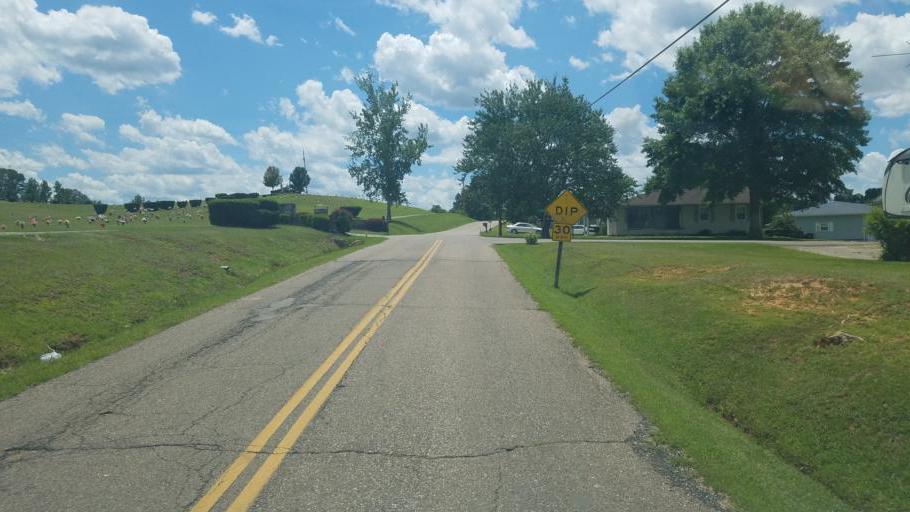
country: US
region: Ohio
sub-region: Gallia County
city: Gallipolis
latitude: 38.7920
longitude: -82.2411
